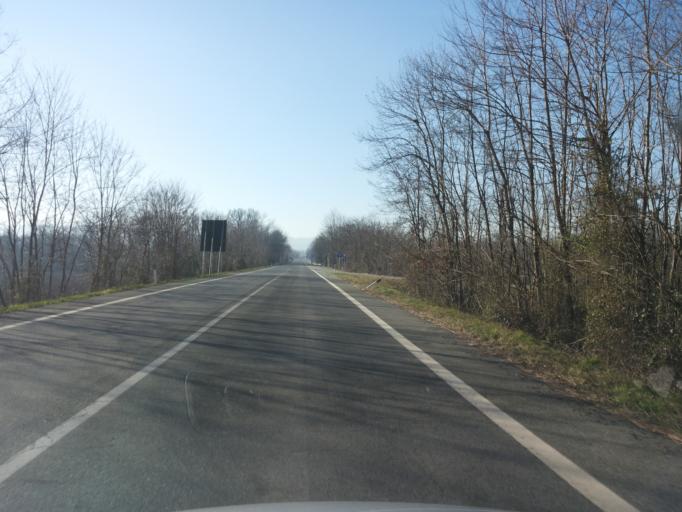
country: IT
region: Piedmont
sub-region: Provincia di Biella
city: Vergnasco
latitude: 45.4832
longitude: 8.1013
